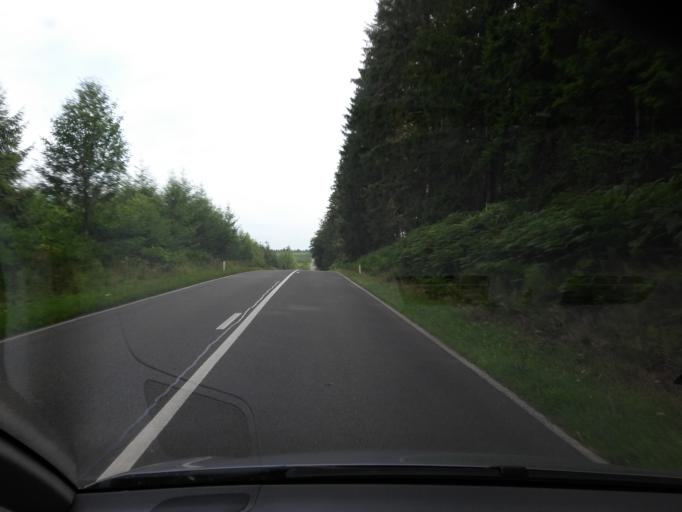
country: BE
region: Wallonia
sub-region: Province du Luxembourg
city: Chiny
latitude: 49.7561
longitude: 5.3159
